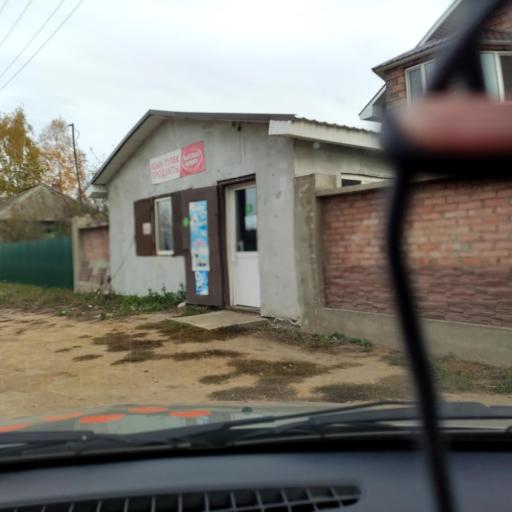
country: RU
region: Bashkortostan
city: Kabakovo
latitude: 54.5268
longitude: 56.0275
